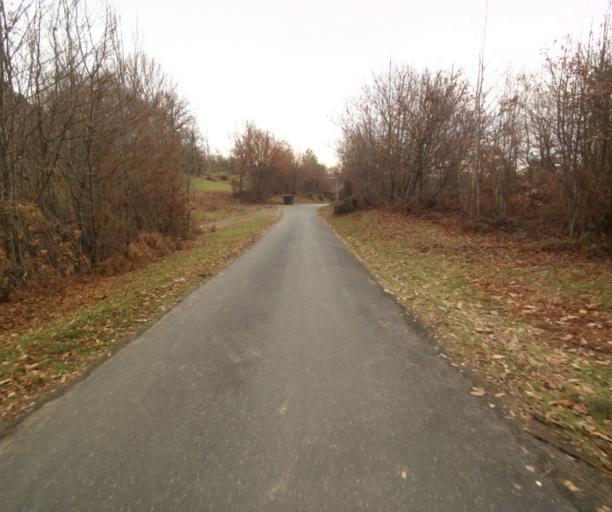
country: FR
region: Limousin
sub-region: Departement de la Correze
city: Chameyrat
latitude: 45.2601
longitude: 1.7060
